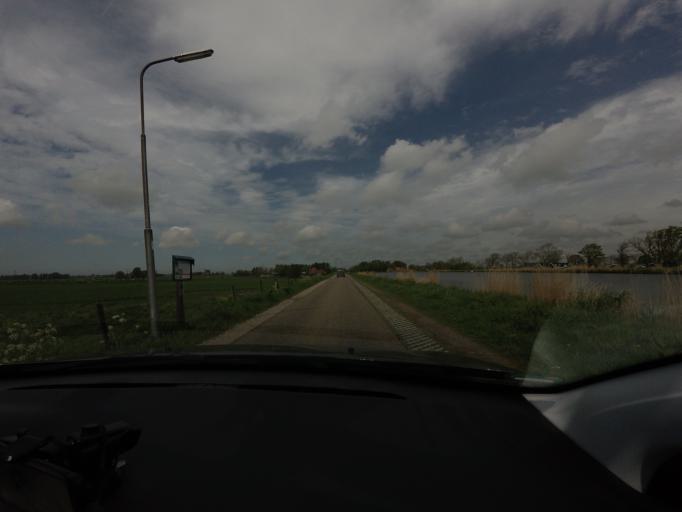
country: NL
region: North Holland
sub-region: Gemeente Zaanstad
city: Zaanstad
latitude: 52.5470
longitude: 4.8080
